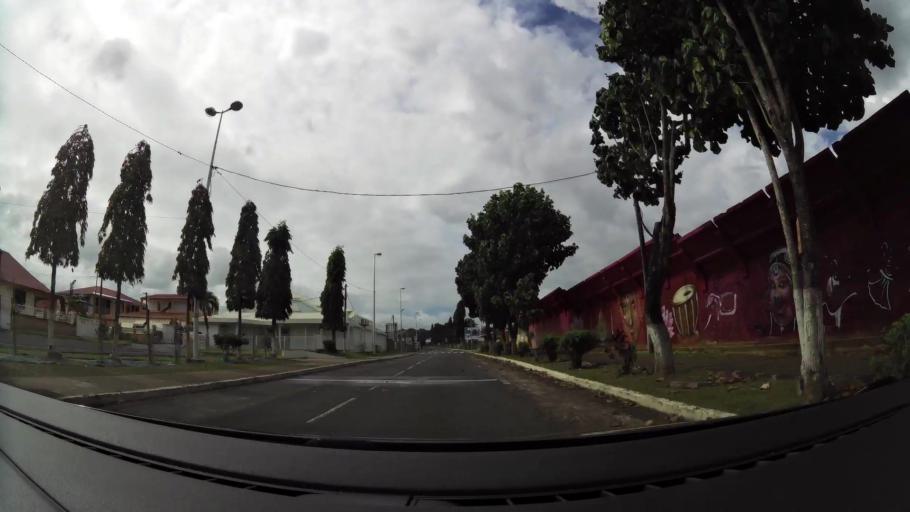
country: GP
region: Guadeloupe
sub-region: Guadeloupe
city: Baie-Mahault
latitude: 16.2623
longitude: -61.5903
